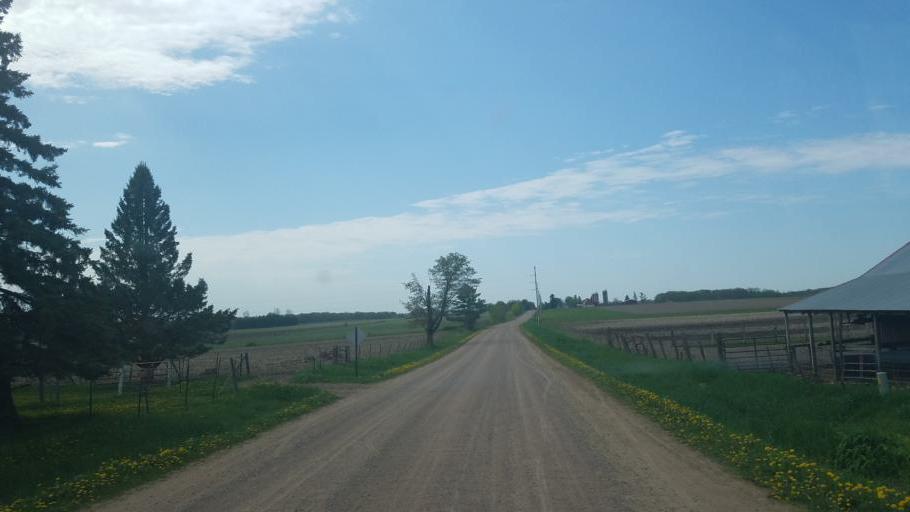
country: US
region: Wisconsin
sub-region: Marathon County
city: Spencer
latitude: 44.6355
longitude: -90.3767
